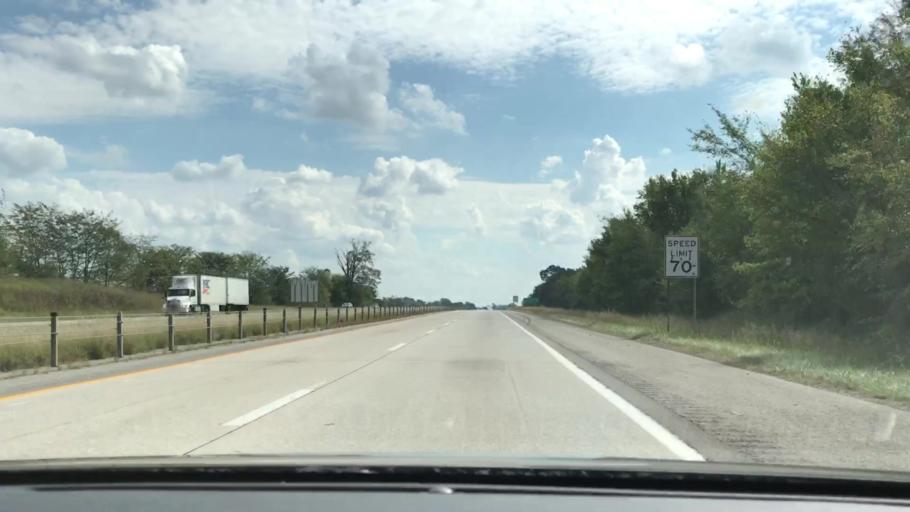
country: US
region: Kentucky
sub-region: Trigg County
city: Cadiz
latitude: 36.8757
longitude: -87.7250
